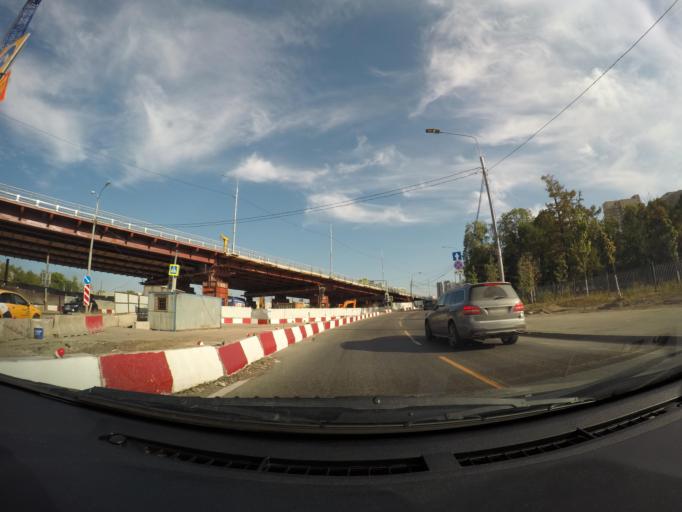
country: RU
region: Moscow
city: Likhobory
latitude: 55.8377
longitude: 37.5703
